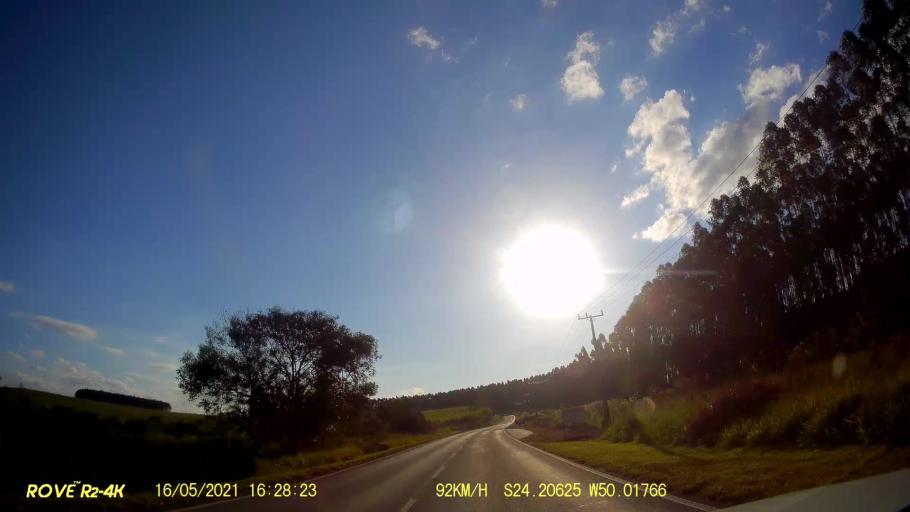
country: BR
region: Parana
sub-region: Jaguariaiva
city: Jaguariaiva
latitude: -24.2062
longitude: -50.0177
